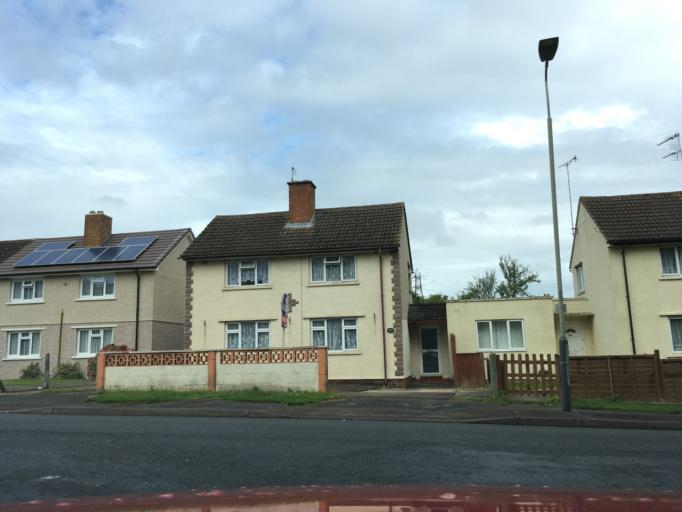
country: GB
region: England
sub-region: Gloucestershire
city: Uckington
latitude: 51.9084
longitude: -2.1181
